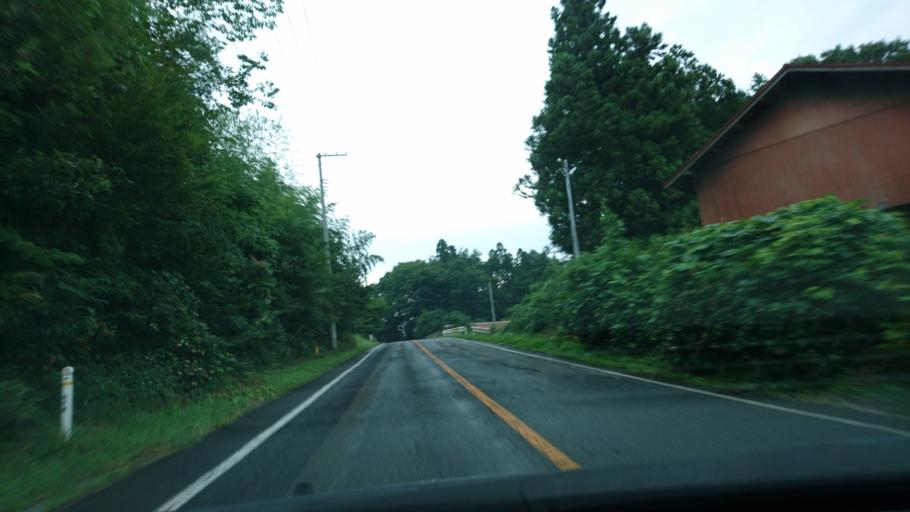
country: JP
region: Iwate
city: Ichinoseki
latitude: 39.0178
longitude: 141.2109
